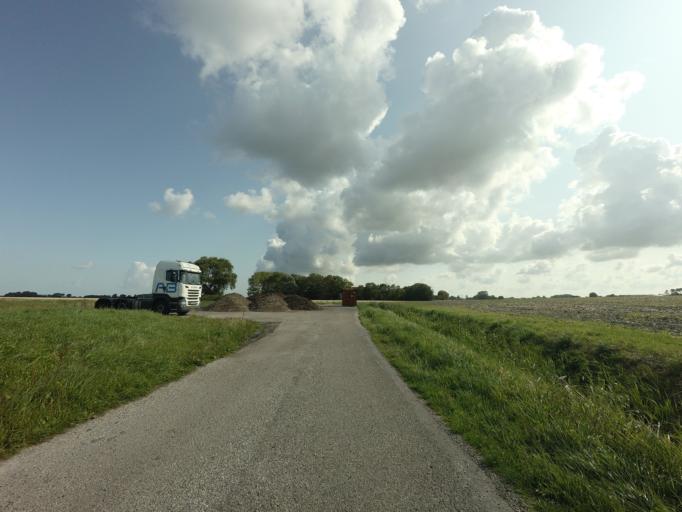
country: NL
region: Friesland
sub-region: Gemeente Franekeradeel
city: Tzummarum
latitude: 53.2435
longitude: 5.5404
